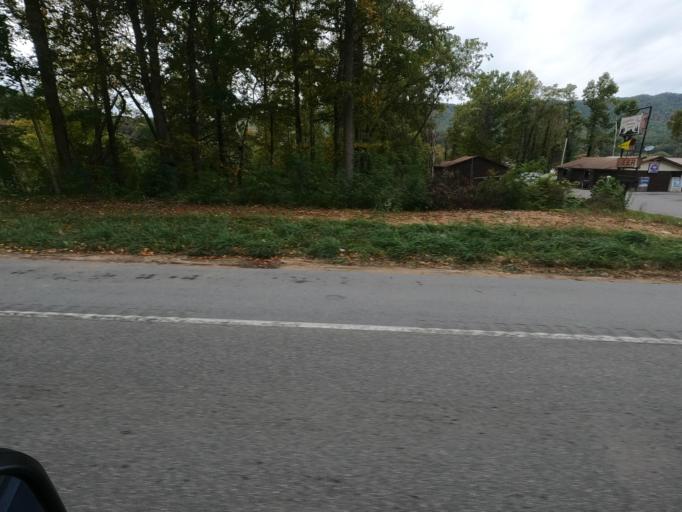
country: US
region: Tennessee
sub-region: Carter County
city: Elizabethton
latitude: 36.2591
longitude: -82.1884
